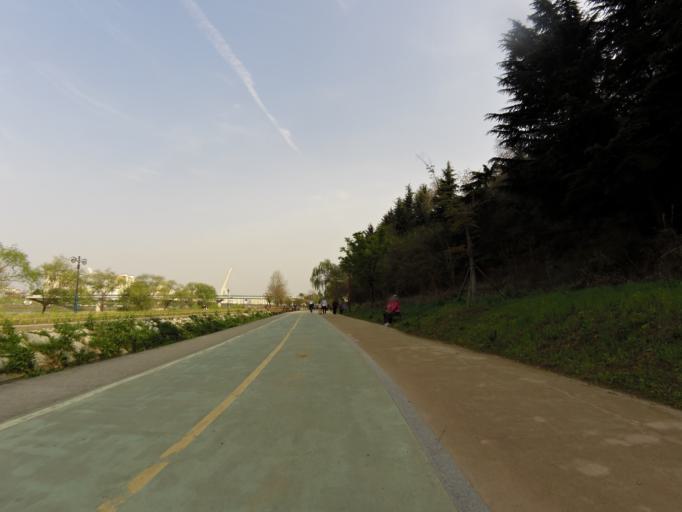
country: KR
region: Daegu
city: Daegu
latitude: 35.8857
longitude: 128.6454
